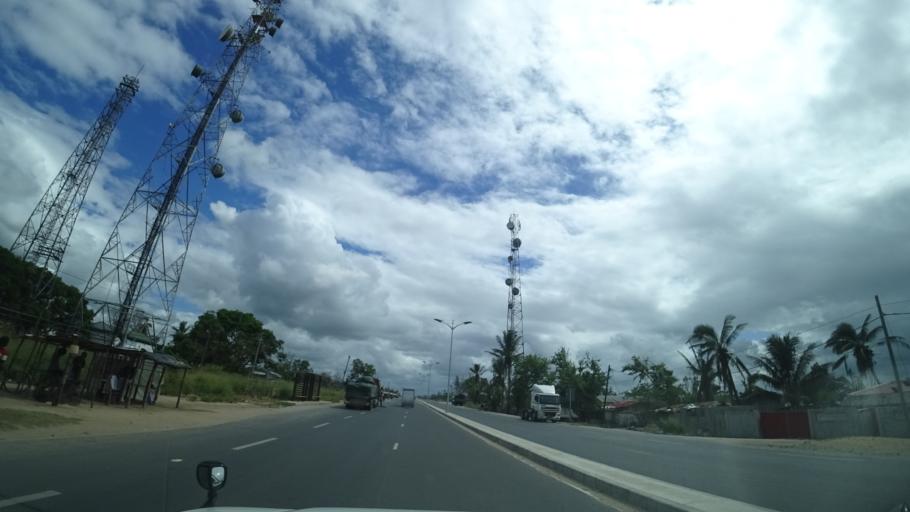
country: MZ
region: Sofala
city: Dondo
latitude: -19.5777
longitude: 34.7244
